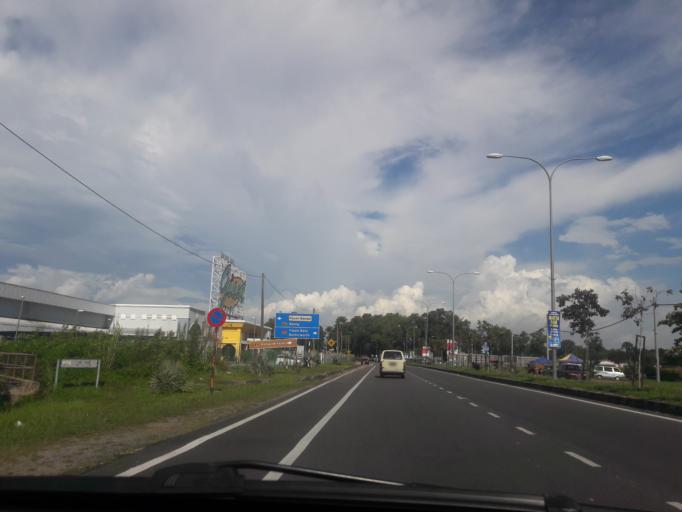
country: MY
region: Kedah
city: Sungai Petani
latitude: 5.6155
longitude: 100.4705
